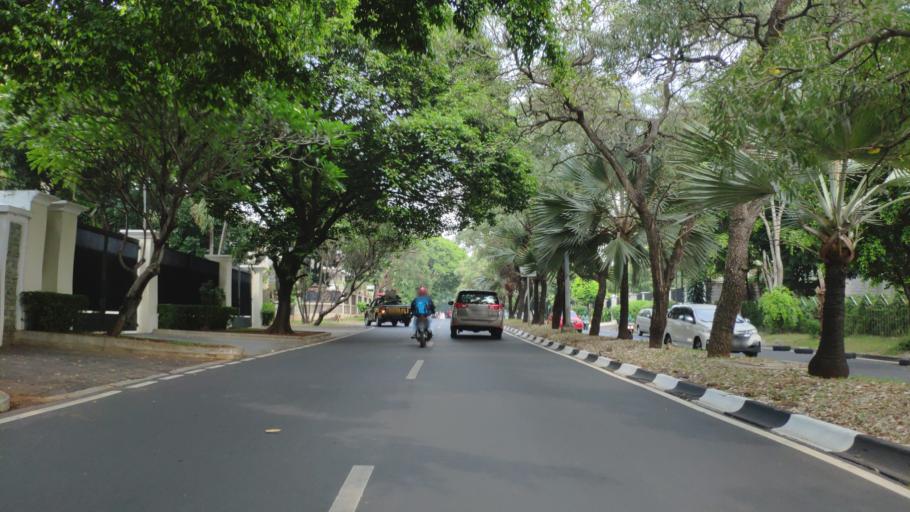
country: ID
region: Banten
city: South Tangerang
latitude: -6.2811
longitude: 106.7830
